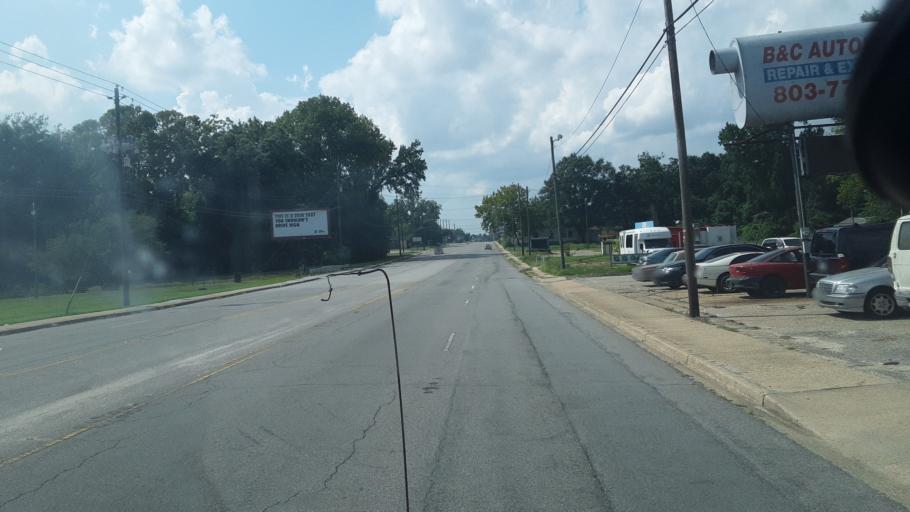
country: US
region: South Carolina
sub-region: Sumter County
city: Sumter
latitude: 33.9391
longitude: -80.3628
